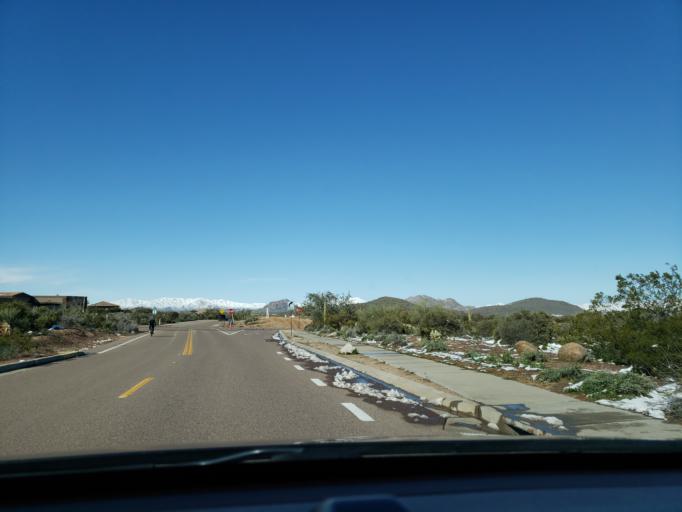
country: US
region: Arizona
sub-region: Maricopa County
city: Carefree
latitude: 33.7260
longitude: -111.8265
